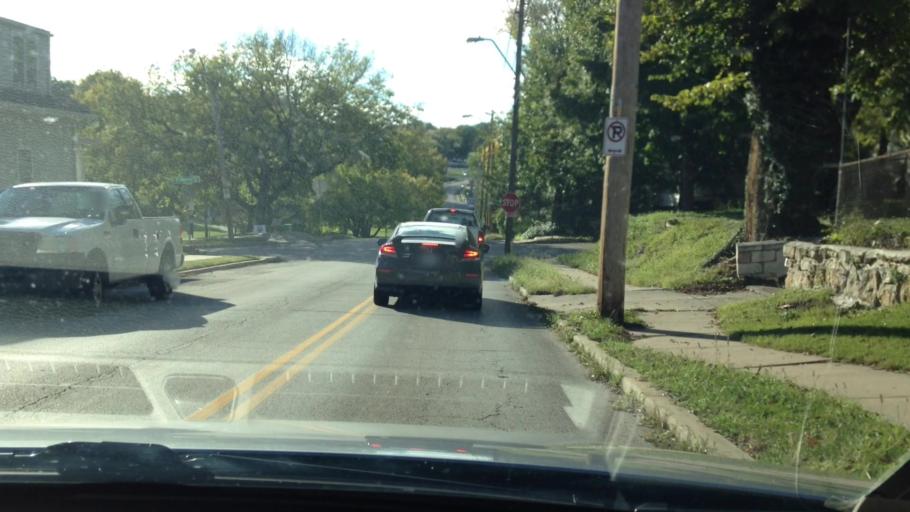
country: US
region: Kansas
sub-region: Johnson County
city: Westwood
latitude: 39.0428
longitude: -94.6047
